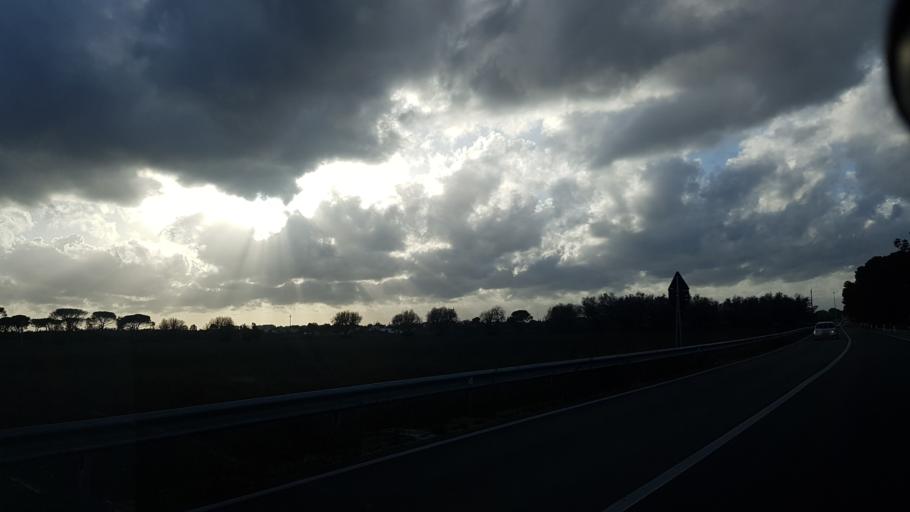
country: IT
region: Apulia
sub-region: Provincia di Brindisi
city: San Pietro Vernotico
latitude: 40.4873
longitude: 18.0188
